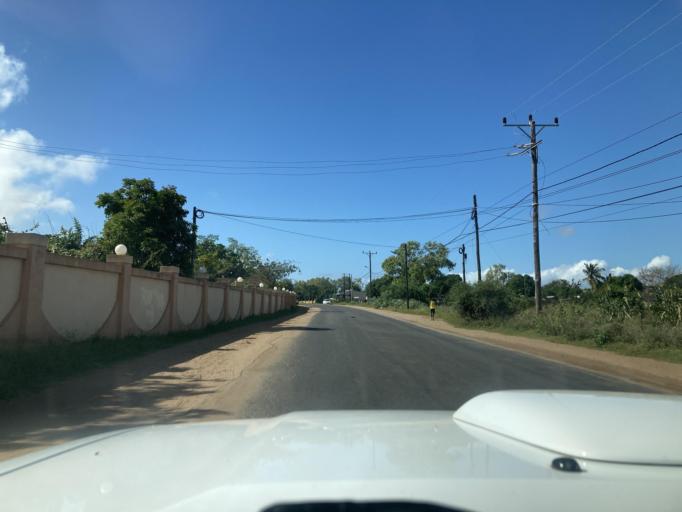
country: MZ
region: Cabo Delgado
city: Pemba
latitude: -12.9645
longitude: 40.5283
